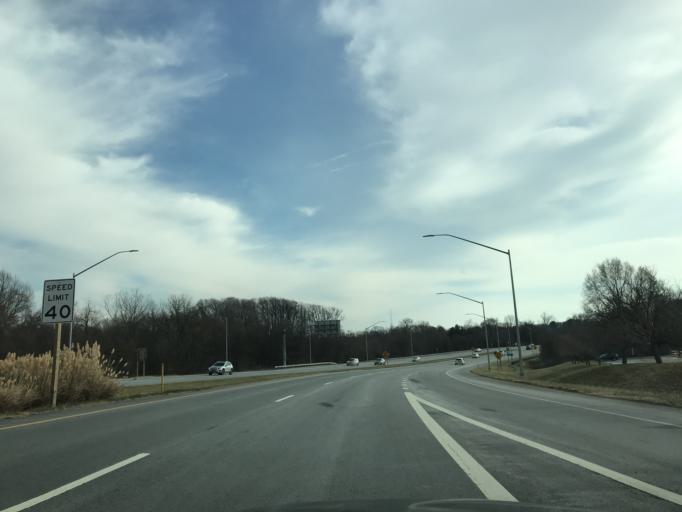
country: US
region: Maryland
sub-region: Howard County
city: Columbia
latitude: 39.2391
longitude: -76.8343
